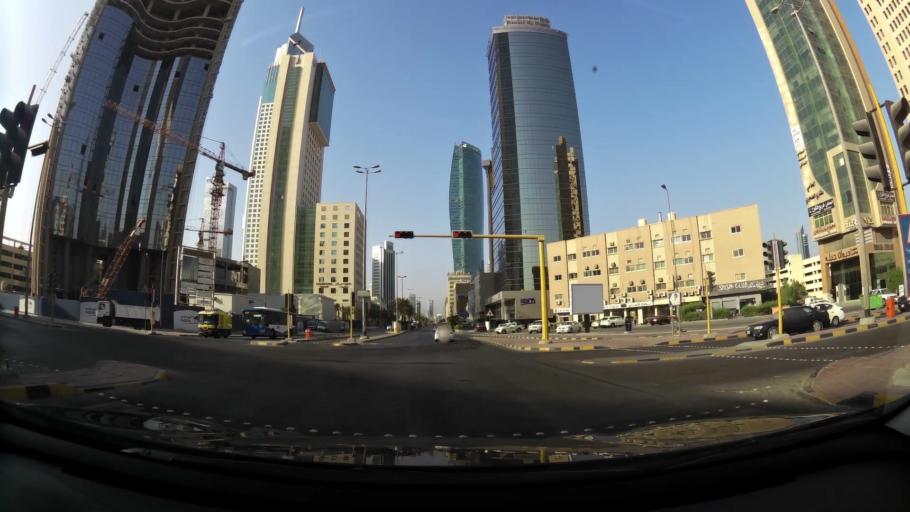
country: KW
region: Al Asimah
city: Kuwait City
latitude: 29.3792
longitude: 47.9919
